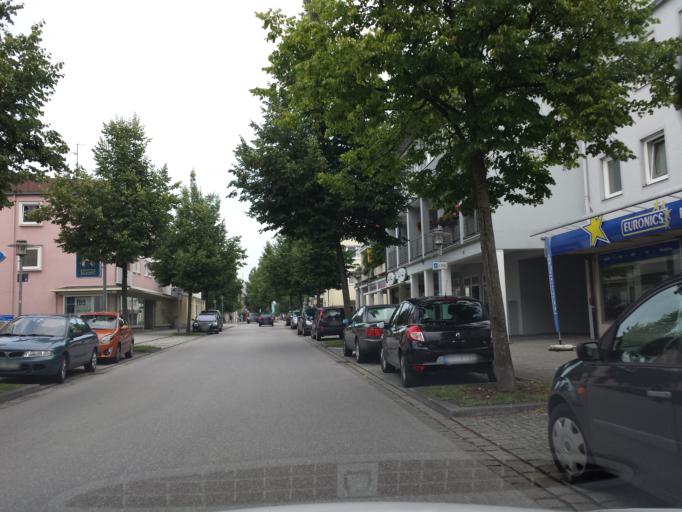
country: DE
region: Bavaria
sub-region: Upper Bavaria
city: Freilassing
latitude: 47.8393
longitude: 12.9801
